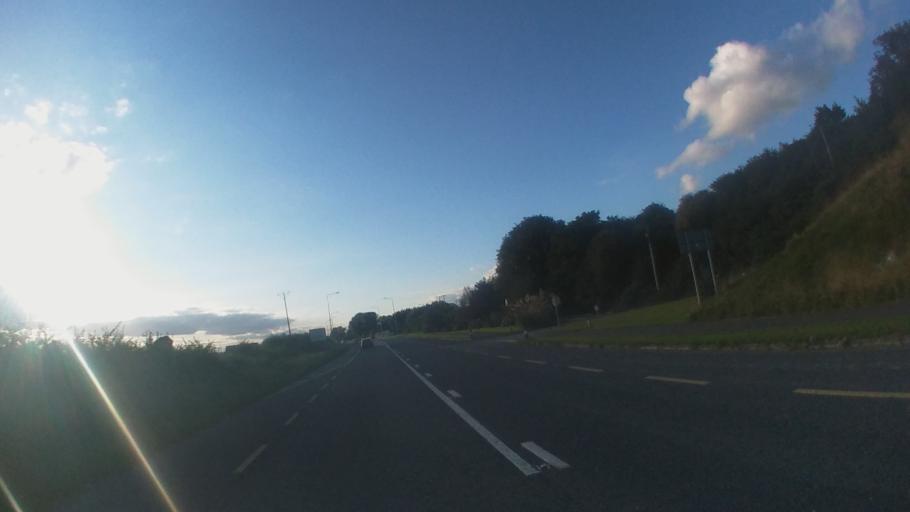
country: IE
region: Leinster
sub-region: Lu
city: Blackrock
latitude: 54.0061
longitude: -6.2873
